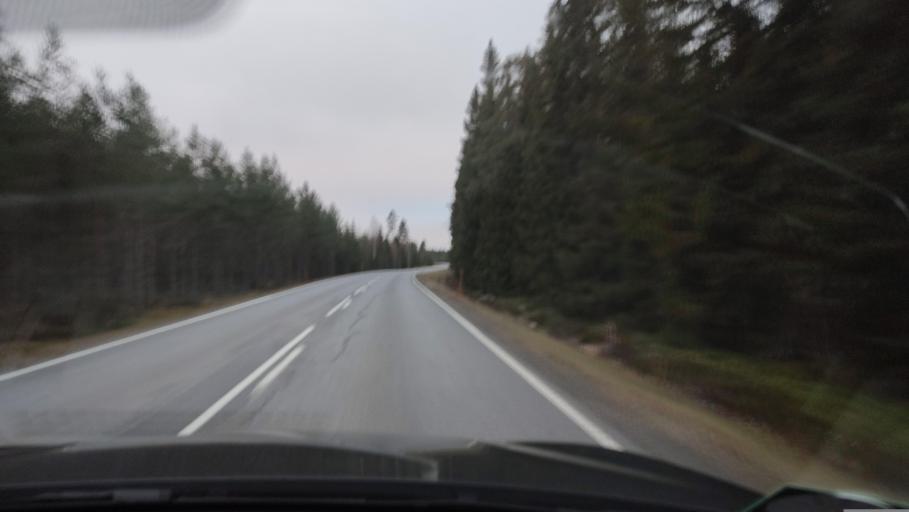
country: FI
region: Southern Ostrobothnia
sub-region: Suupohja
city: Karijoki
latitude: 62.3254
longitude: 21.8636
